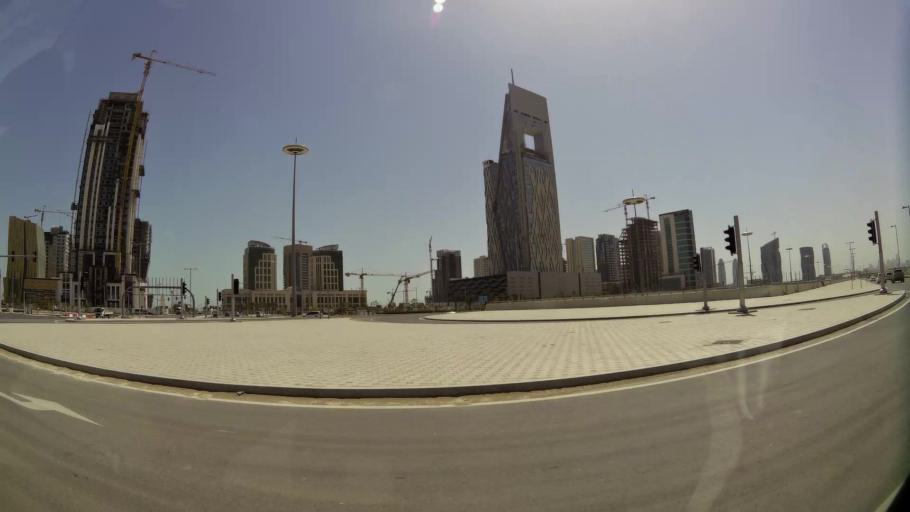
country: QA
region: Baladiyat ad Dawhah
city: Doha
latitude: 25.3932
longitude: 51.5166
